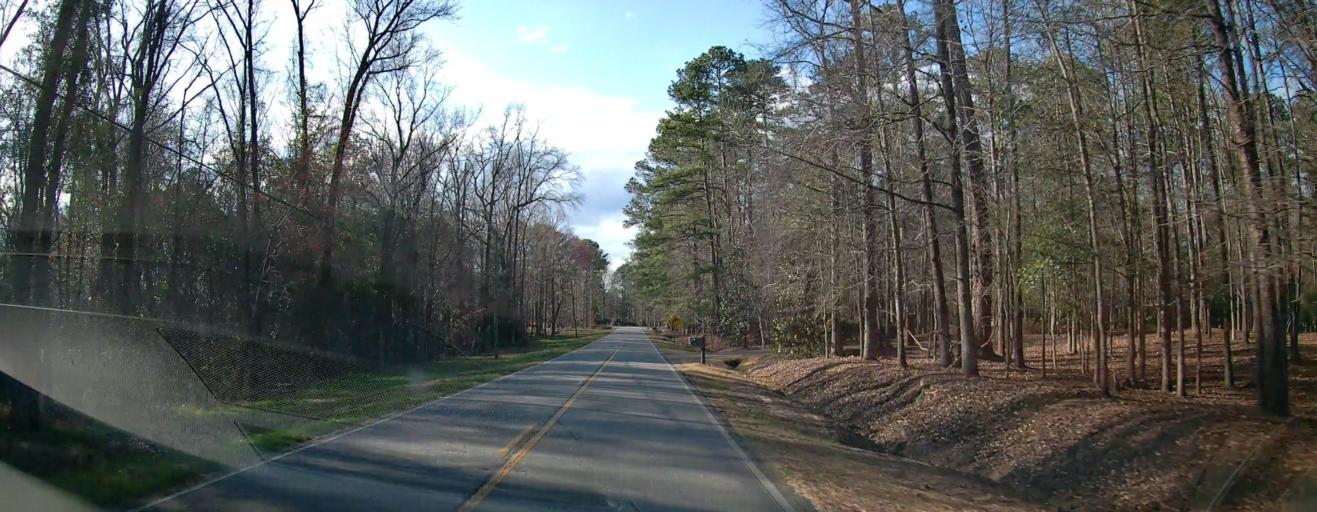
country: US
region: Georgia
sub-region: Harris County
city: Hamilton
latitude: 32.5707
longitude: -84.8076
